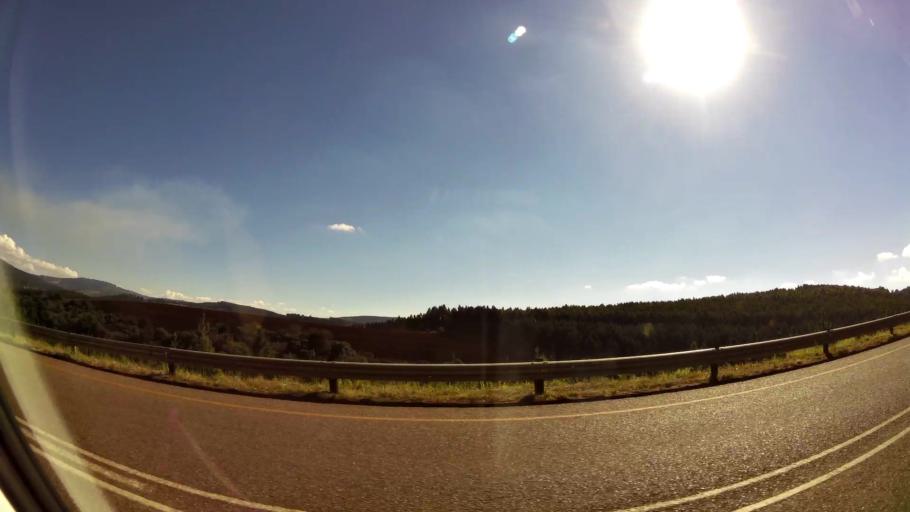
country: ZA
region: Limpopo
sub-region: Capricorn District Municipality
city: Mankoeng
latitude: -23.9301
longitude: 29.9572
